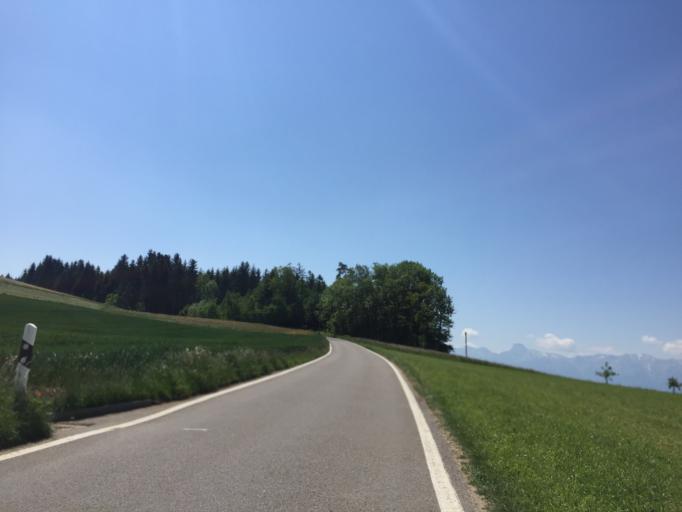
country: CH
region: Bern
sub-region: Bern-Mittelland District
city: Taegertschi
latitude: 46.8694
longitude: 7.5847
